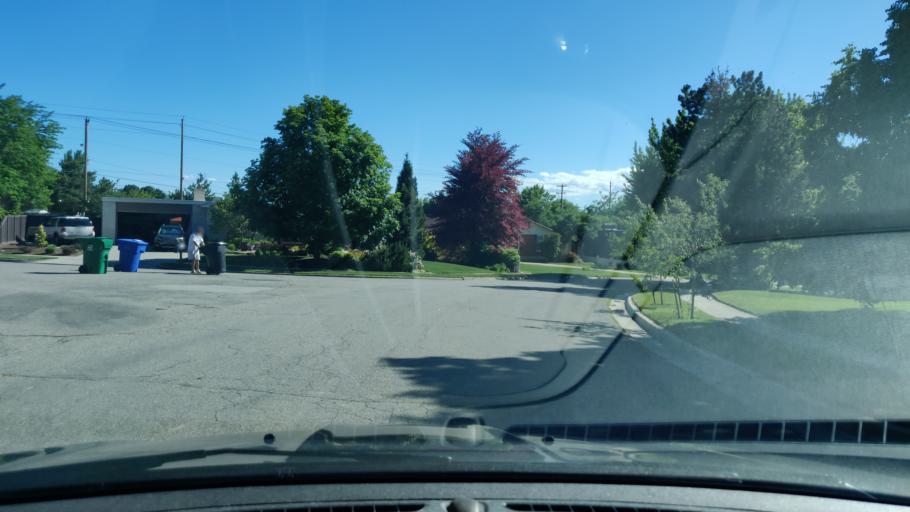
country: US
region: Utah
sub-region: Salt Lake County
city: Cottonwood Heights
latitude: 40.6103
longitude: -111.8062
